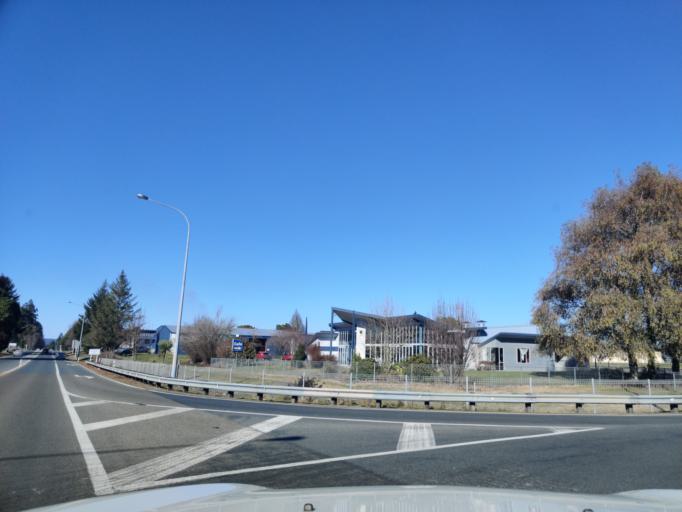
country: NZ
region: Waikato
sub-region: South Waikato District
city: Tokoroa
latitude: -38.2263
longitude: 175.8771
